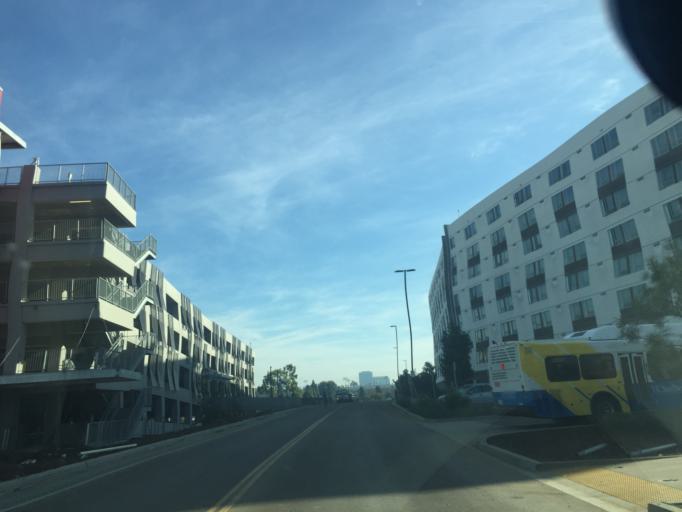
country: US
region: California
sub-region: San Diego County
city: La Jolla
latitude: 32.8758
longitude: -117.2235
